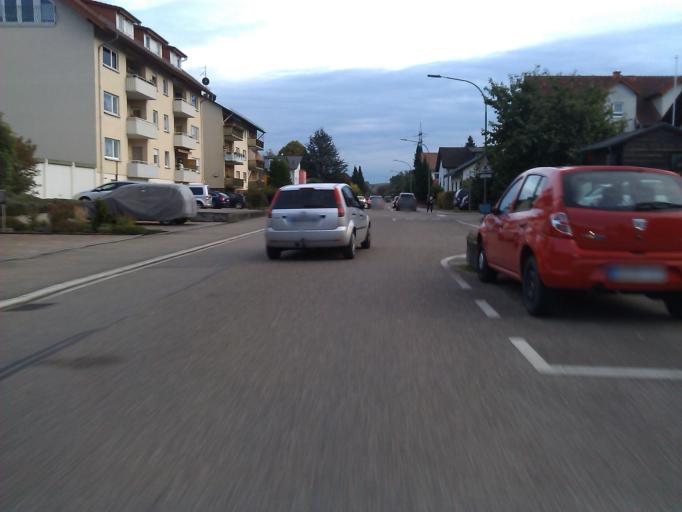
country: DE
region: Baden-Wuerttemberg
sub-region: Karlsruhe Region
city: Meckesheim
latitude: 49.3167
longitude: 8.8148
